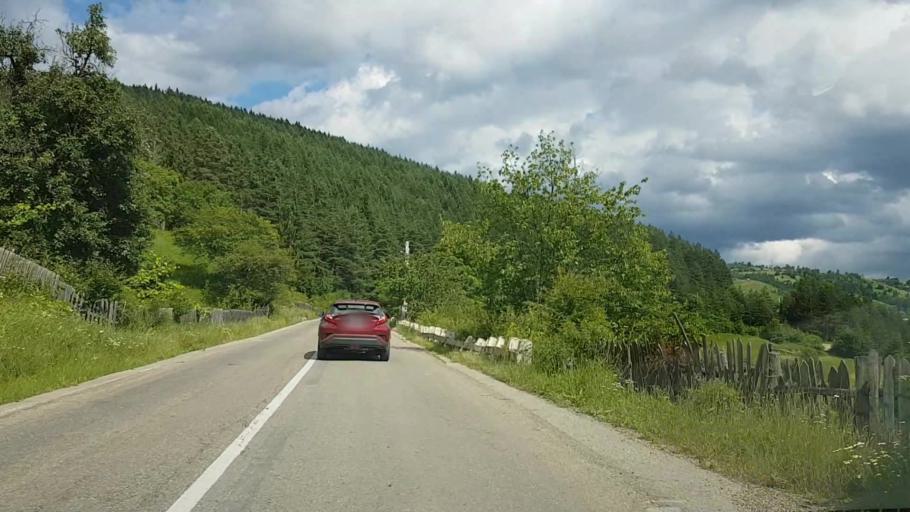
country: RO
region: Neamt
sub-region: Comuna Hangu
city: Hangu
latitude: 47.0123
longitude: 26.0811
